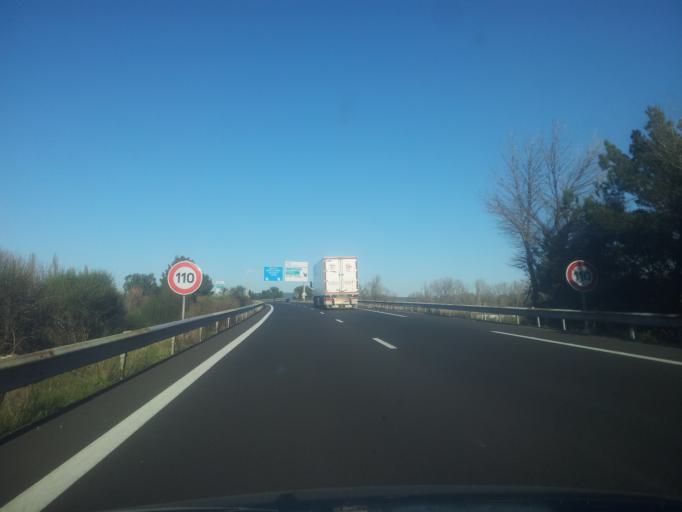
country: FR
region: Provence-Alpes-Cote d'Azur
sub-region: Departement du Vaucluse
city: Orange
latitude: 44.1261
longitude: 4.7921
